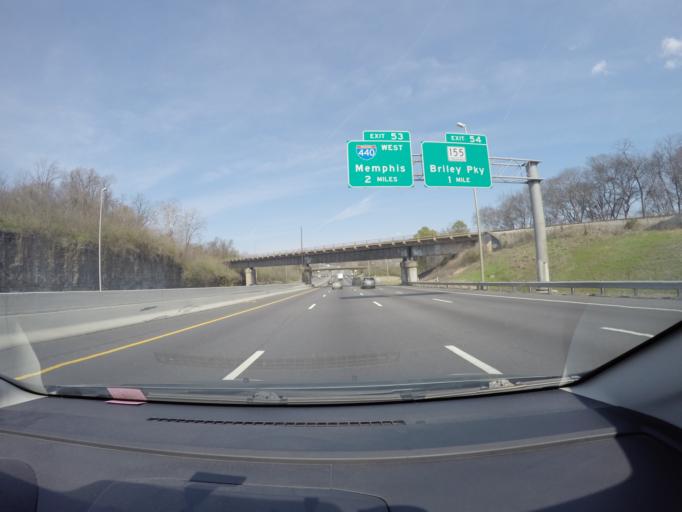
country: US
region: Tennessee
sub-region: Davidson County
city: Oak Hill
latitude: 36.0959
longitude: -86.7077
